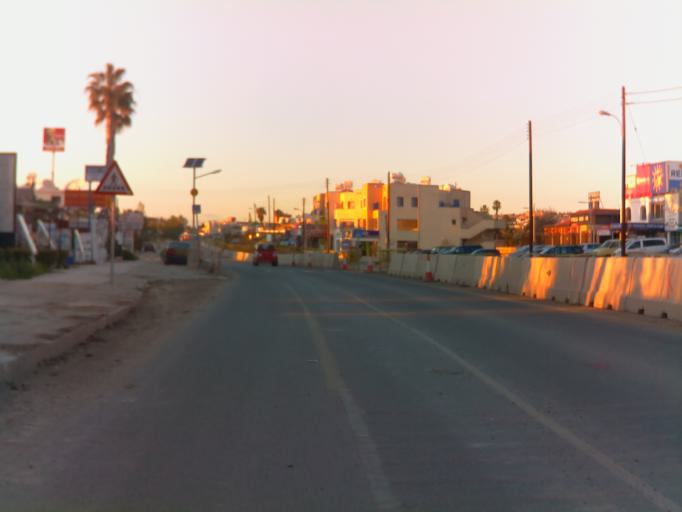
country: CY
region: Pafos
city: Paphos
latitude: 34.7710
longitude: 32.4104
